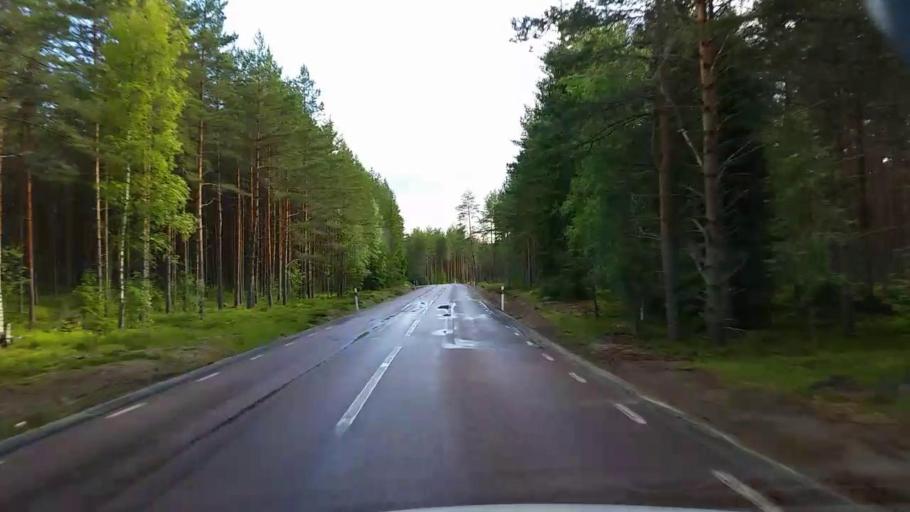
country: SE
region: Vaestmanland
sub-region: Fagersta Kommun
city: Fagersta
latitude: 59.9029
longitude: 15.8211
